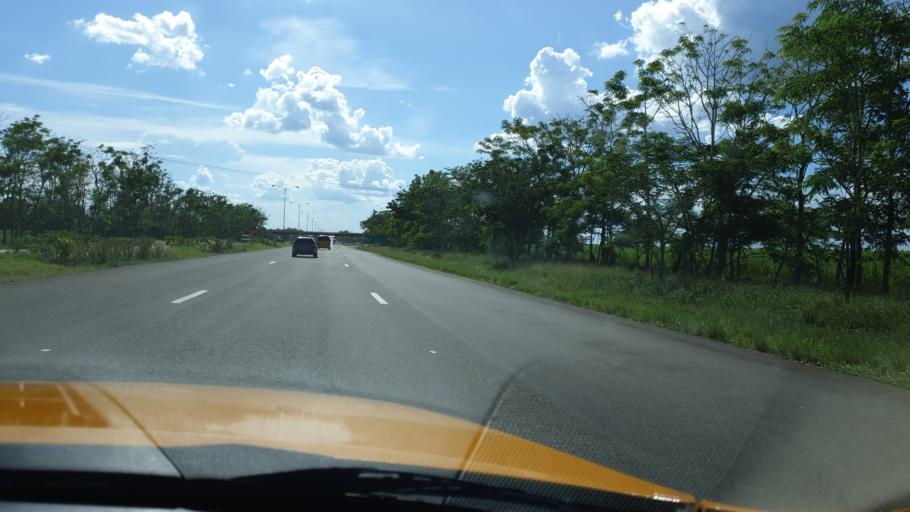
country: CU
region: Cienfuegos
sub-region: Municipio de Aguada de Pasajeros
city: Aguada de Pasajeros
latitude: 22.4028
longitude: -80.8585
